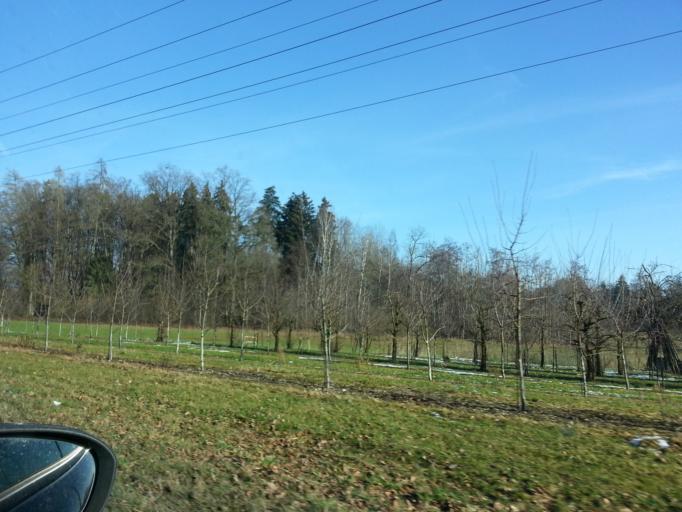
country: DE
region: Baden-Wuerttemberg
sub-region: Tuebingen Region
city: Immenstaad am Bodensee
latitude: 47.6777
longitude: 9.3835
